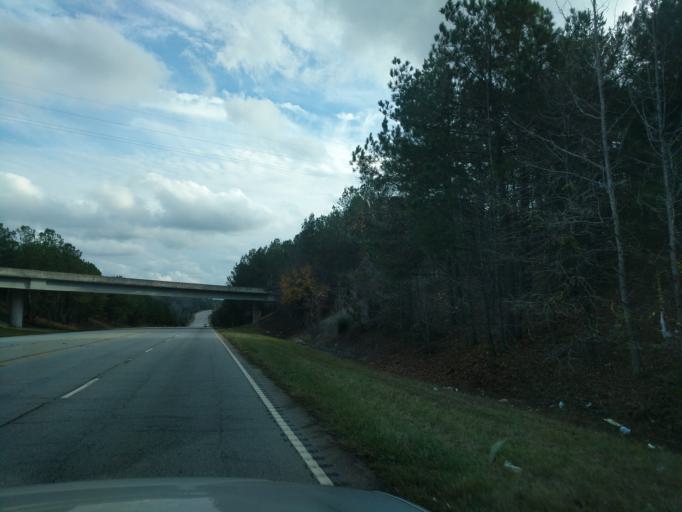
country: US
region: South Carolina
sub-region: Greenwood County
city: Ware Shoals
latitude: 34.4176
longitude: -82.2319
